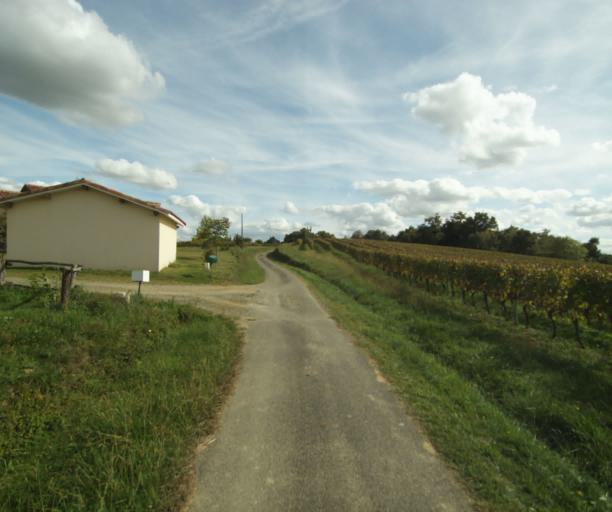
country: FR
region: Midi-Pyrenees
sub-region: Departement du Gers
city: Eauze
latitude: 43.8360
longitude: 0.1411
